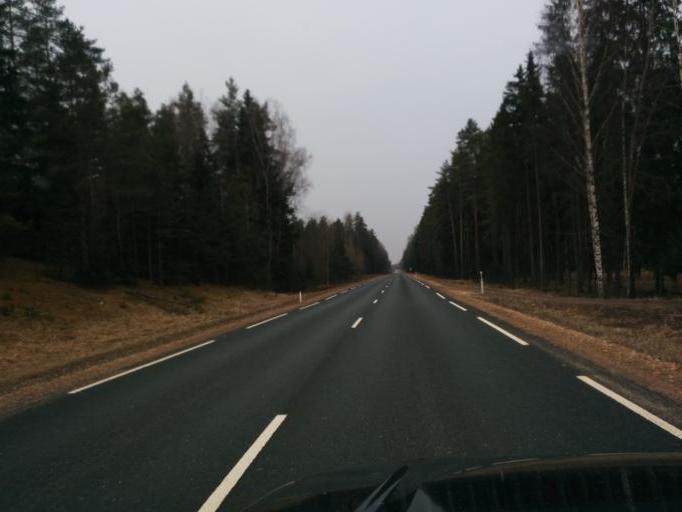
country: LV
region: Ikskile
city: Ikskile
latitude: 56.8047
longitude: 24.4984
